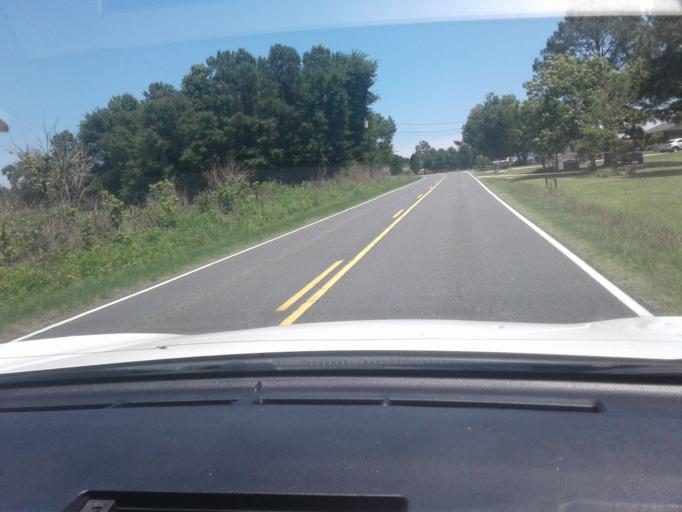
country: US
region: North Carolina
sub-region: Harnett County
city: Lillington
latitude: 35.3896
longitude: -78.7956
